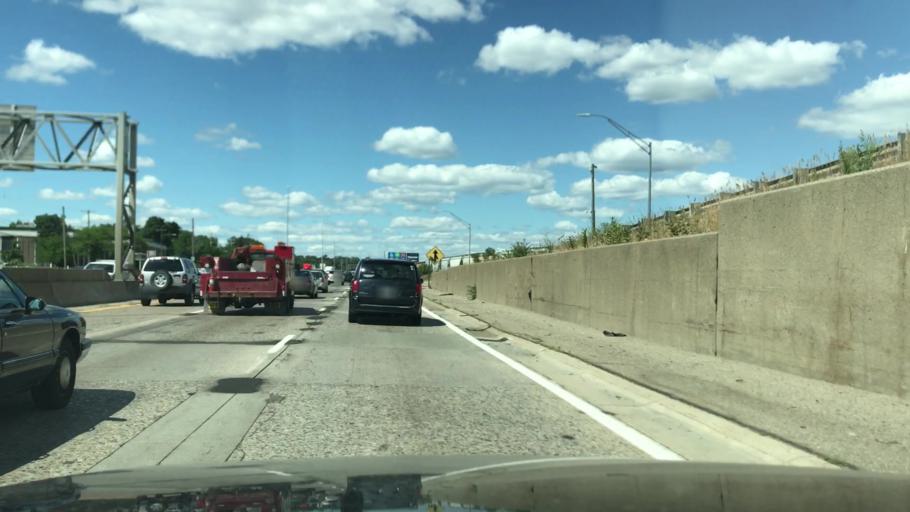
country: US
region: Michigan
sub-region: Kent County
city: Wyoming
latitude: 42.9287
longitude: -85.6815
